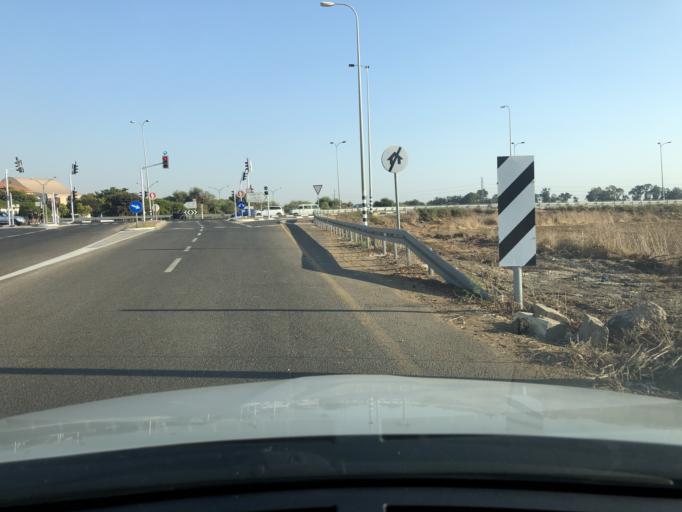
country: IL
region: Central District
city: Hod HaSharon
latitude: 32.1344
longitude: 34.9090
